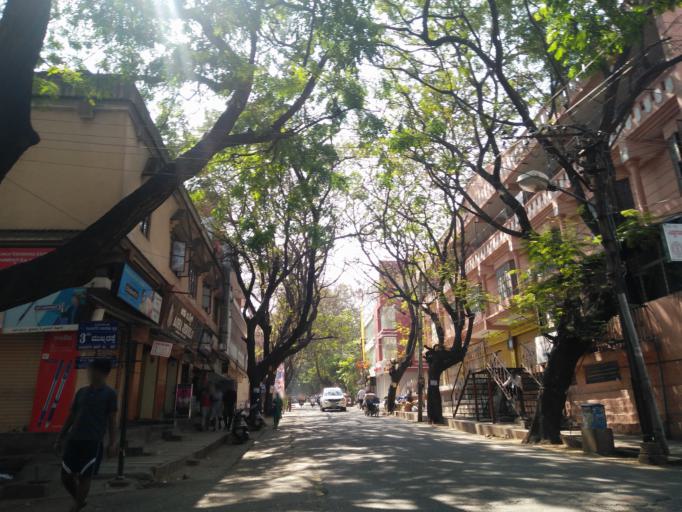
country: IN
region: Karnataka
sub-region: Bangalore Urban
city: Bangalore
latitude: 12.9723
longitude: 77.5441
